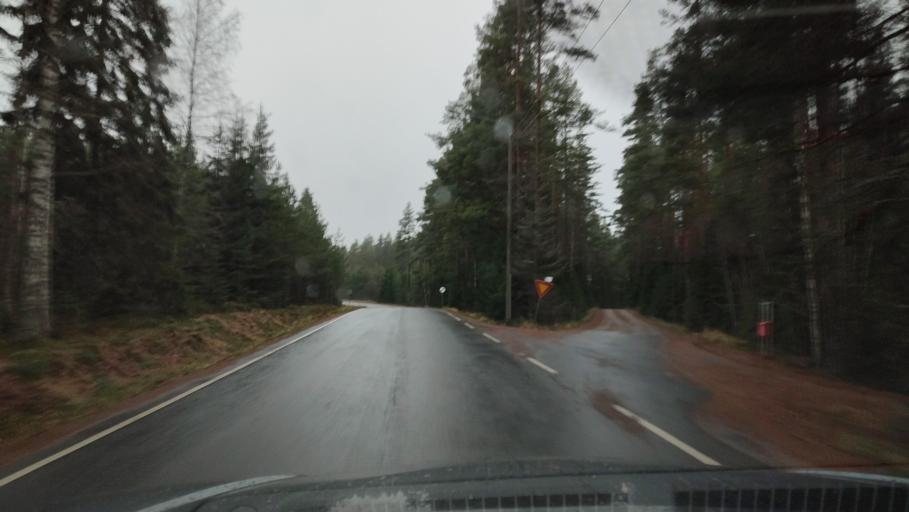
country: FI
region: Southern Ostrobothnia
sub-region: Suupohja
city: Karijoki
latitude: 62.1358
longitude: 21.6719
